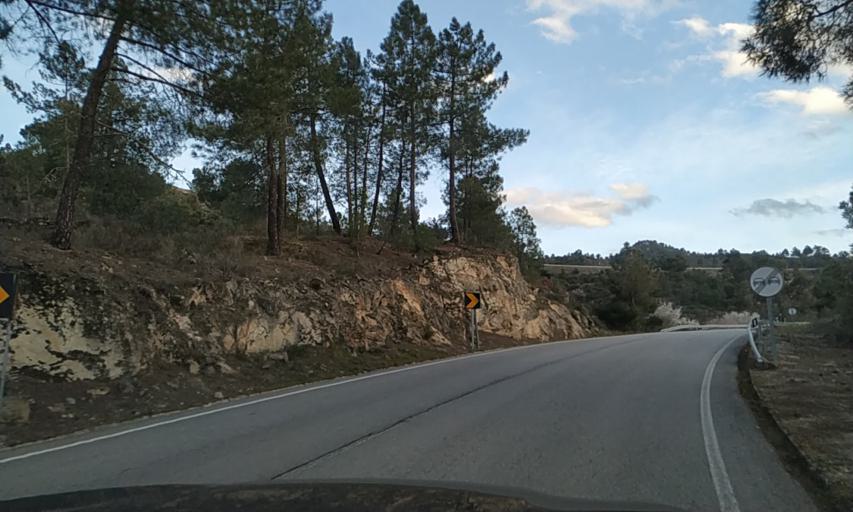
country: PT
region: Braganca
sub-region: Carrazeda de Ansiaes
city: Carrazeda de Anciaes
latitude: 41.2916
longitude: -7.3372
